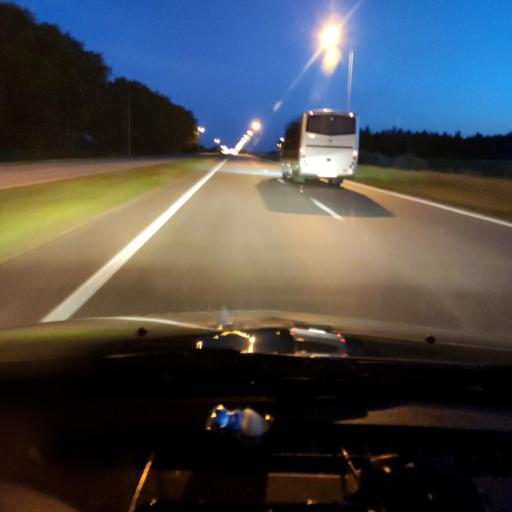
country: RU
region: Belgorod
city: Skorodnoye
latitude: 51.1474
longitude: 37.2826
